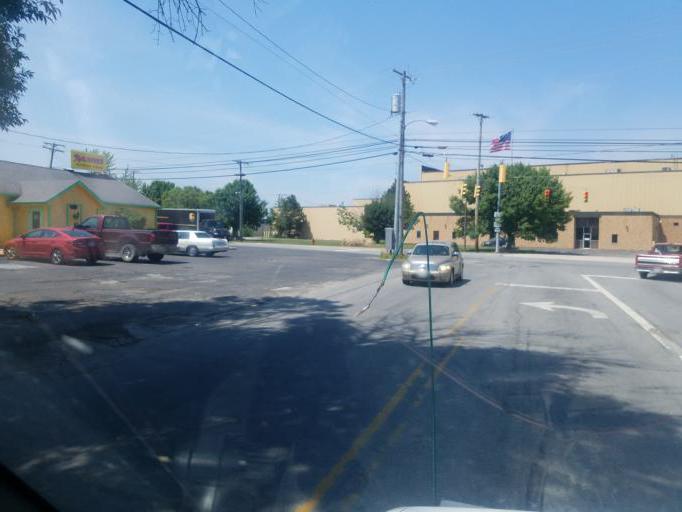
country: US
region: Ohio
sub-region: Auglaize County
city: Saint Marys
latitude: 40.5438
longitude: -84.4157
